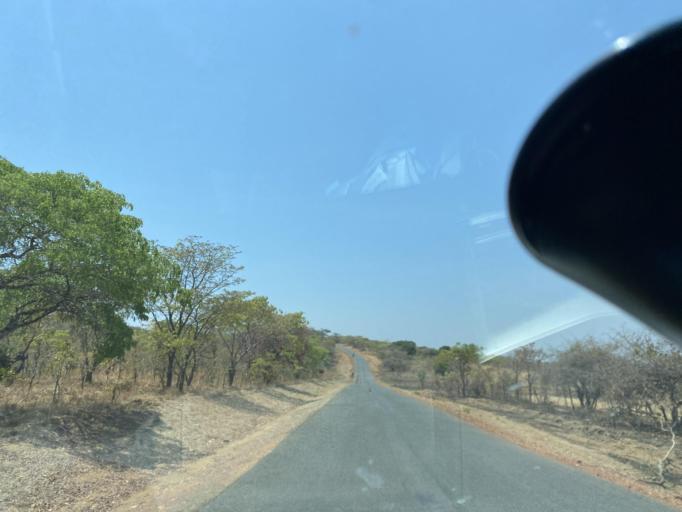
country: ZM
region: Lusaka
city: Kafue
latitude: -15.8407
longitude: 28.4084
